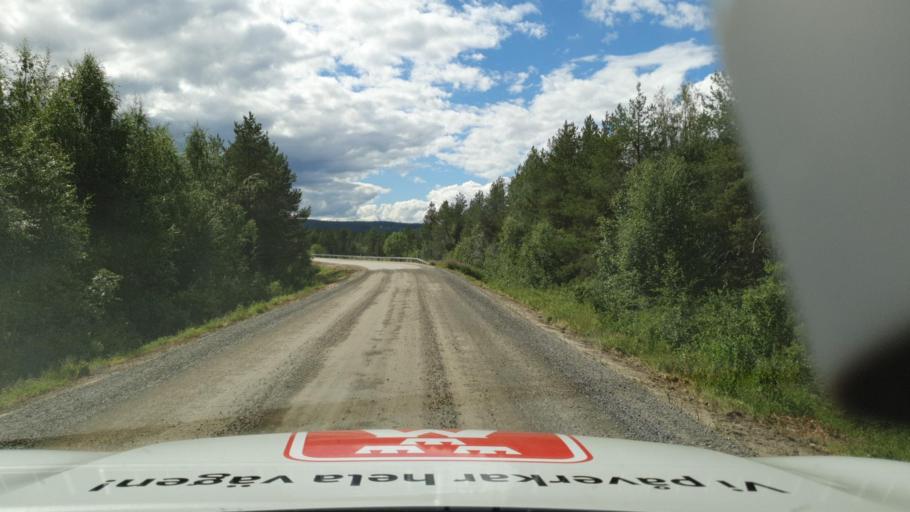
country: SE
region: Vaesterbotten
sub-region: Sorsele Kommun
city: Sorsele
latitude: 65.6035
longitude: 17.4280
